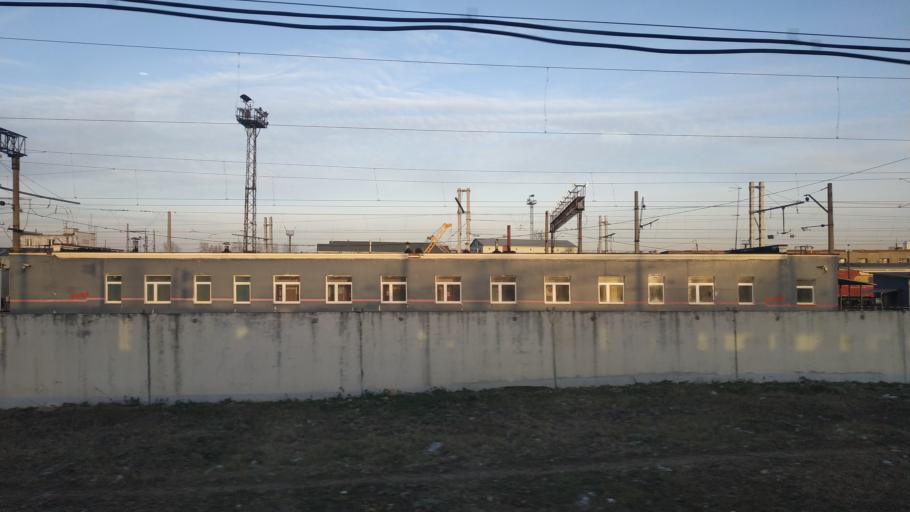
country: RU
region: Moscow
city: Sokol'niki
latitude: 55.7893
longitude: 37.6448
